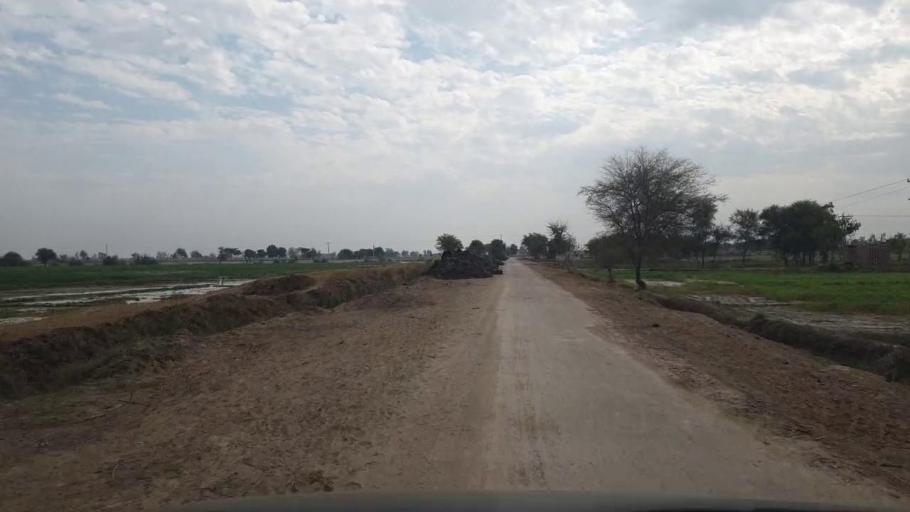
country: PK
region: Sindh
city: Sakrand
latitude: 26.0216
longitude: 68.4285
